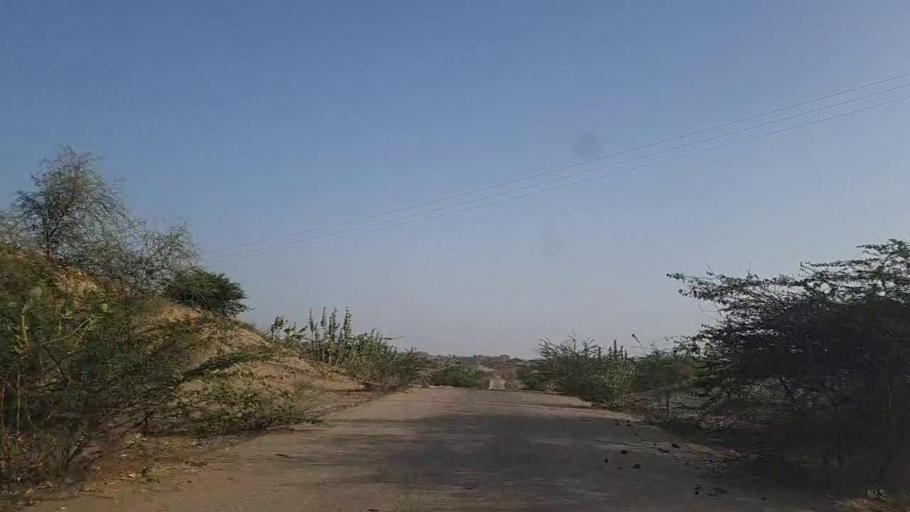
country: PK
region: Sindh
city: Diplo
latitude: 24.6071
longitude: 69.3784
